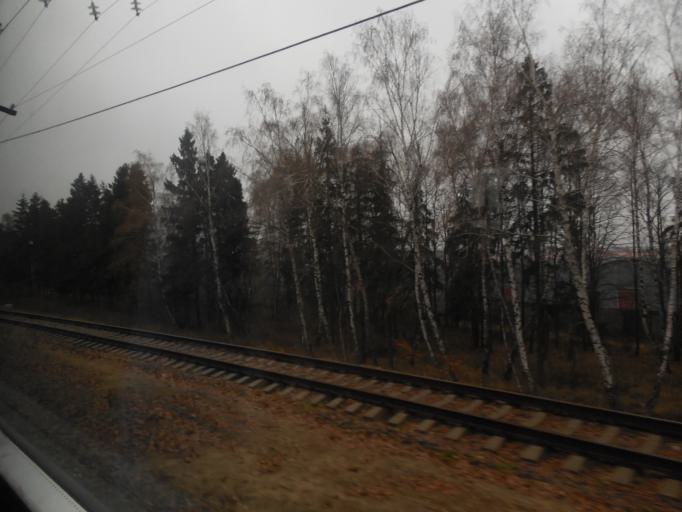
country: RU
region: Moskovskaya
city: Belyye Stolby
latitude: 55.3400
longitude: 37.8459
